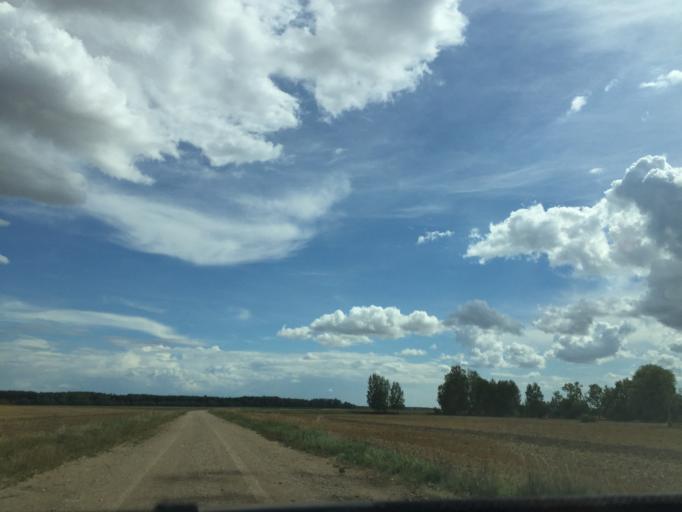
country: LT
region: Siauliu apskritis
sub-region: Joniskis
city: Joniskis
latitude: 56.3568
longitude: 23.6300
